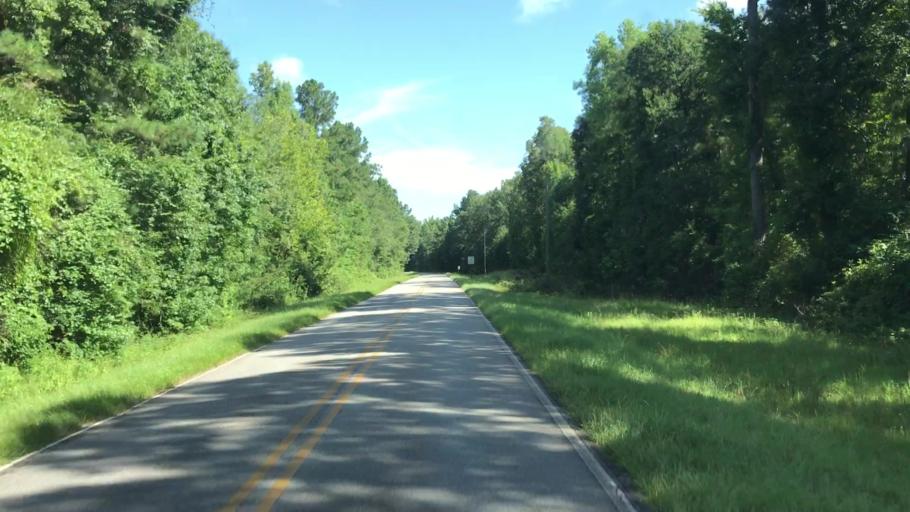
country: US
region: Georgia
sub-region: Jefferson County
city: Wadley
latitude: 32.8155
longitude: -82.3762
